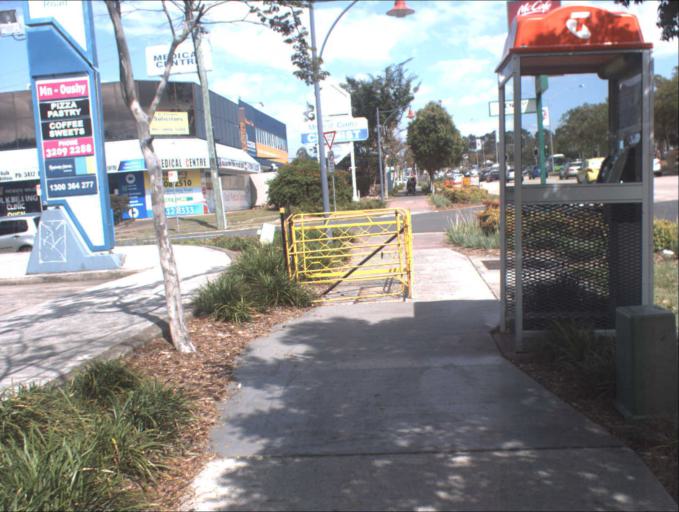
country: AU
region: Queensland
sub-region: Logan
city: Logan City
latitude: -27.6417
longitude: 153.1113
